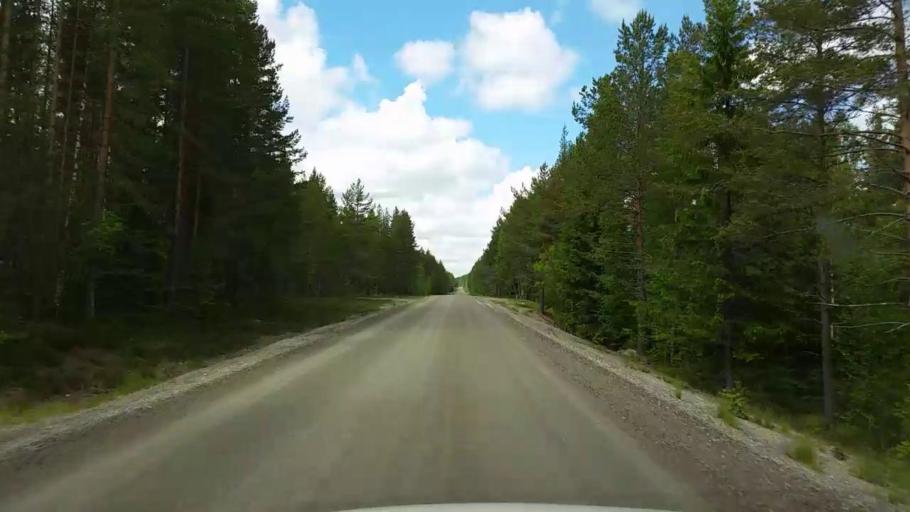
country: SE
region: Gaevleborg
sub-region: Bollnas Kommun
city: Kilafors
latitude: 61.0319
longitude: 16.3715
